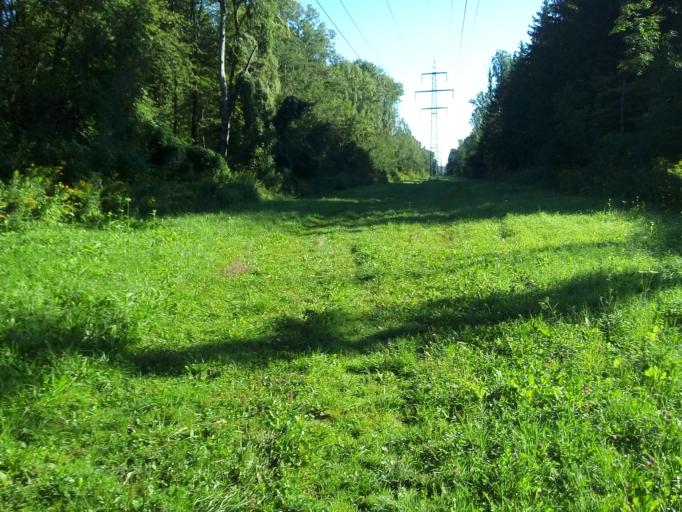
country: DE
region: Bavaria
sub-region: Upper Bavaria
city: Garching bei Munchen
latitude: 48.2256
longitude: 11.6569
